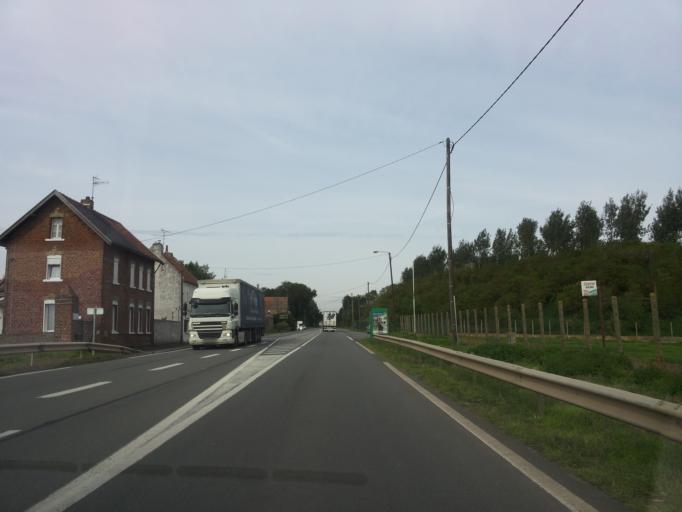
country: FR
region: Nord-Pas-de-Calais
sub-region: Departement du Nord
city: Lecluse
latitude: 50.2284
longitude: 3.0183
